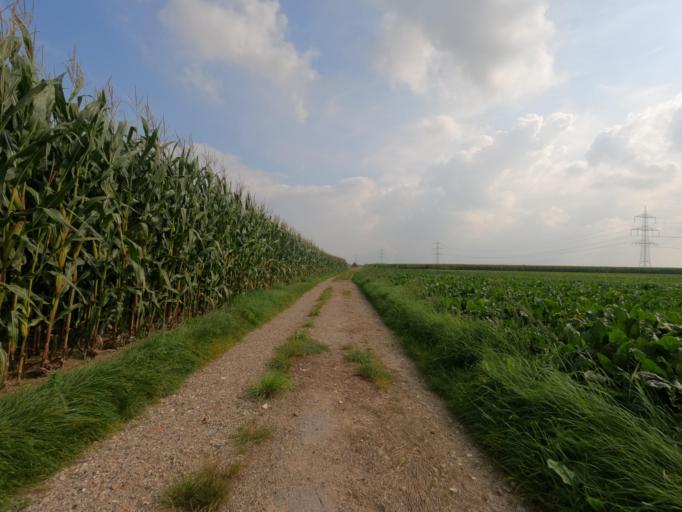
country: DE
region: North Rhine-Westphalia
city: Geilenkirchen
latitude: 50.9693
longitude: 6.1536
